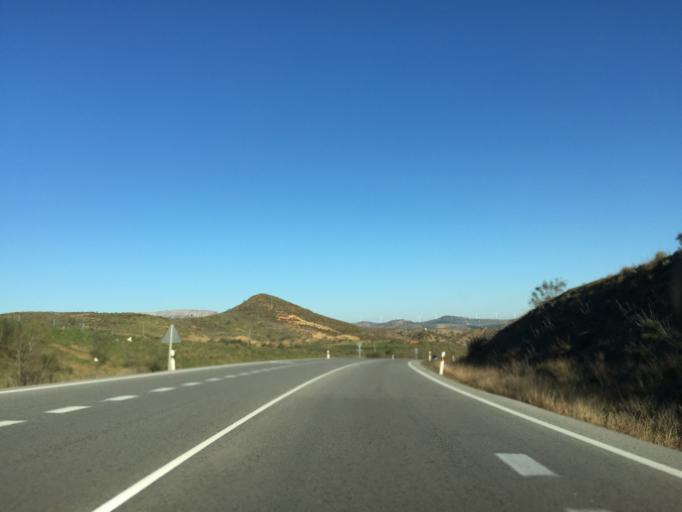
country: ES
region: Andalusia
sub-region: Provincia de Malaga
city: Ardales
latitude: 36.8625
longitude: -4.8403
